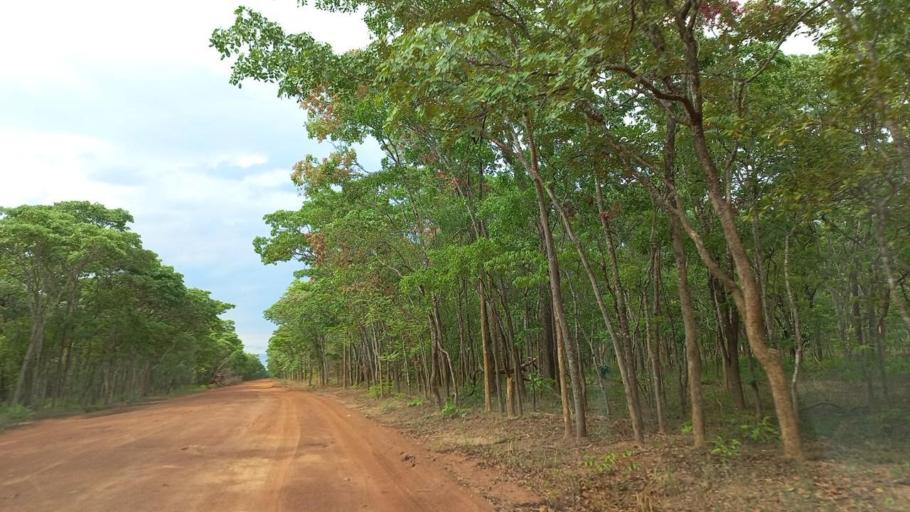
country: ZM
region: North-Western
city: Kalengwa
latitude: -13.3990
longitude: 25.0672
